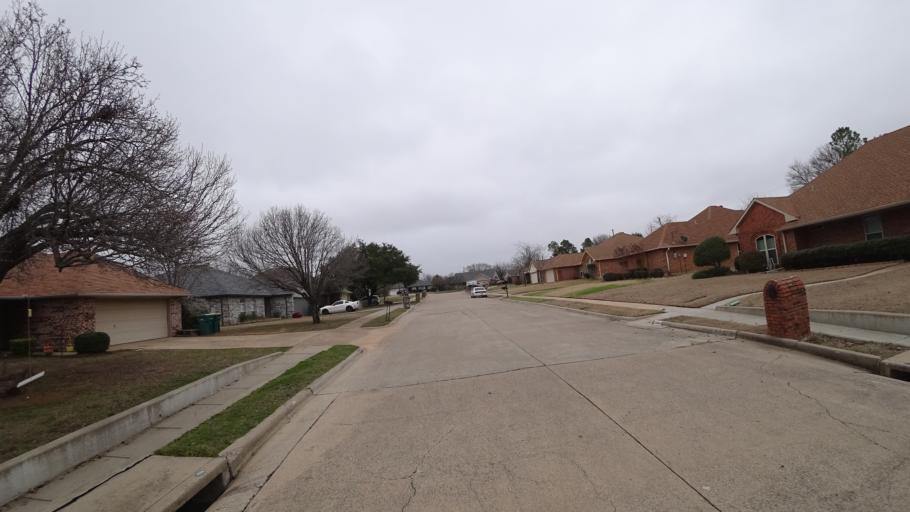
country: US
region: Texas
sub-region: Denton County
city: Lewisville
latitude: 33.0538
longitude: -97.0058
